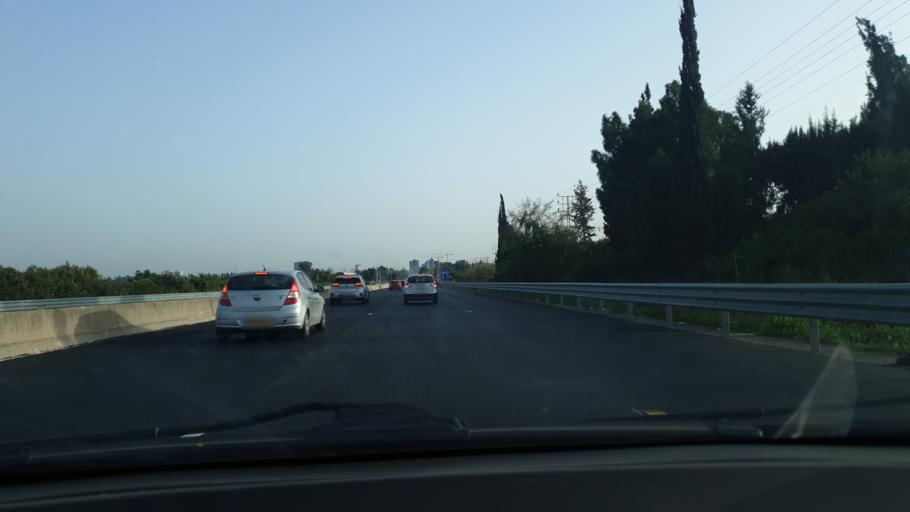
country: IL
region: Central District
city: Ra'anana
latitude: 32.2236
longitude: 34.8828
